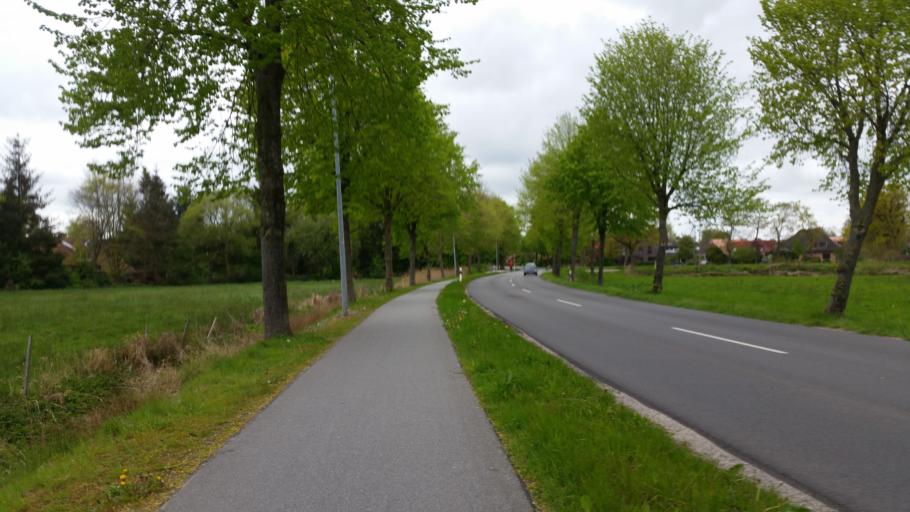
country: DE
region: Lower Saxony
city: Aurich
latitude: 53.4772
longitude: 7.4577
